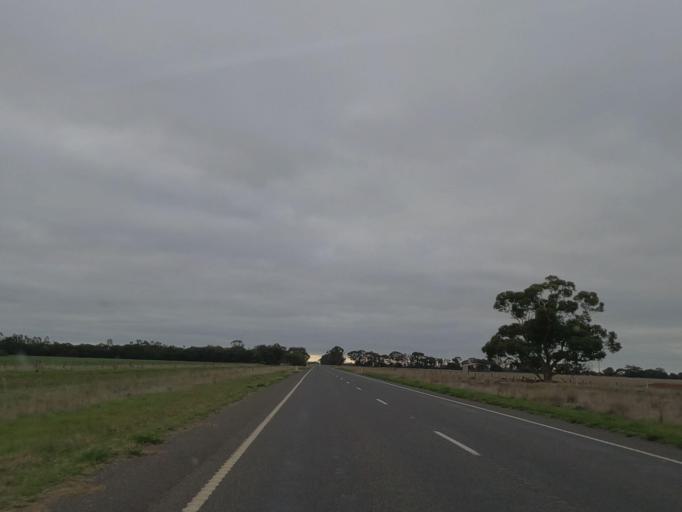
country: AU
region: Victoria
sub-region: Greater Bendigo
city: Long Gully
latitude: -36.0569
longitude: 143.9477
